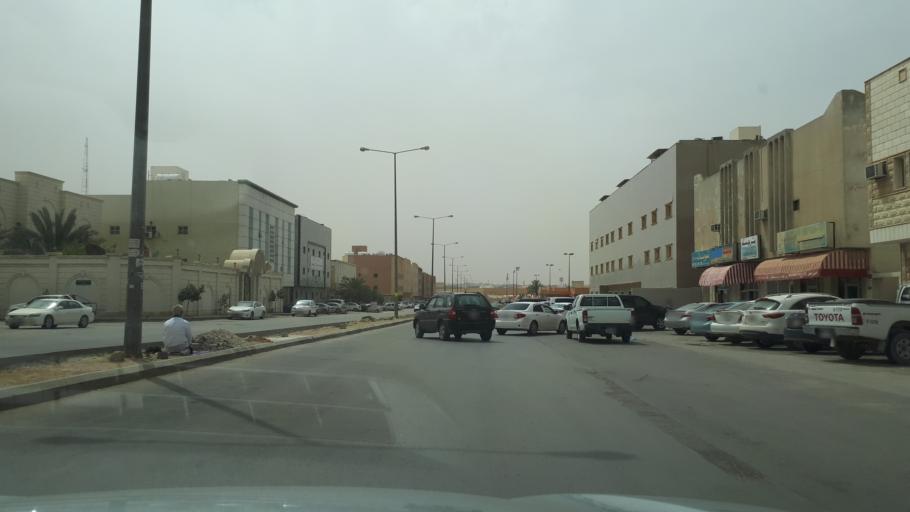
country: SA
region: Ar Riyad
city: Riyadh
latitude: 24.7508
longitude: 46.6384
